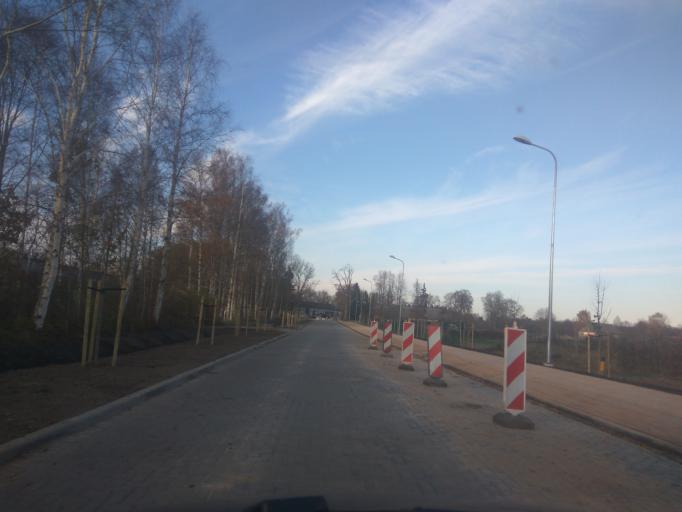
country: LV
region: Kuldigas Rajons
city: Kuldiga
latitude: 56.9843
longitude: 21.9493
